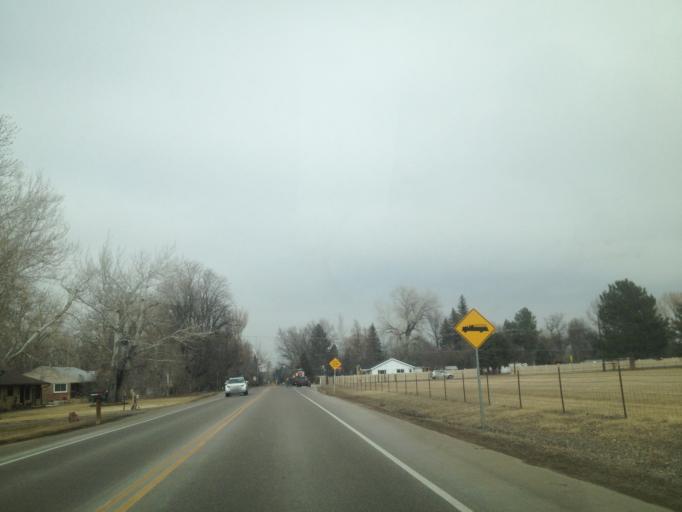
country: US
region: Colorado
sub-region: Boulder County
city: Boulder
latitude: 40.0025
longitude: -105.2125
